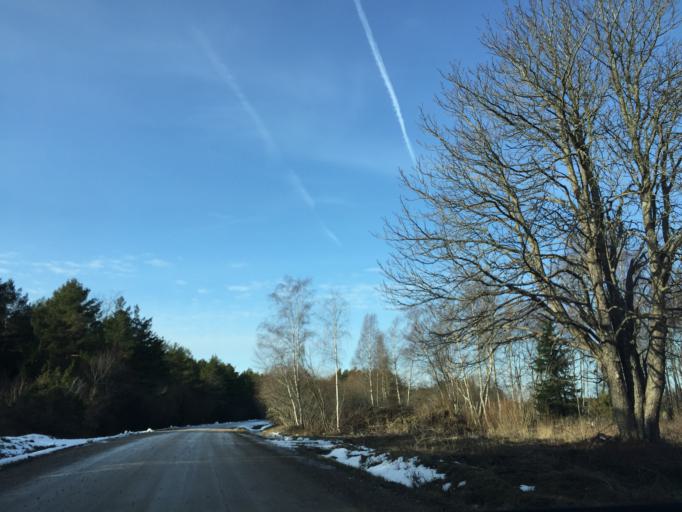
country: EE
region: Saare
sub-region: Kuressaare linn
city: Kuressaare
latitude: 58.3675
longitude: 22.0269
